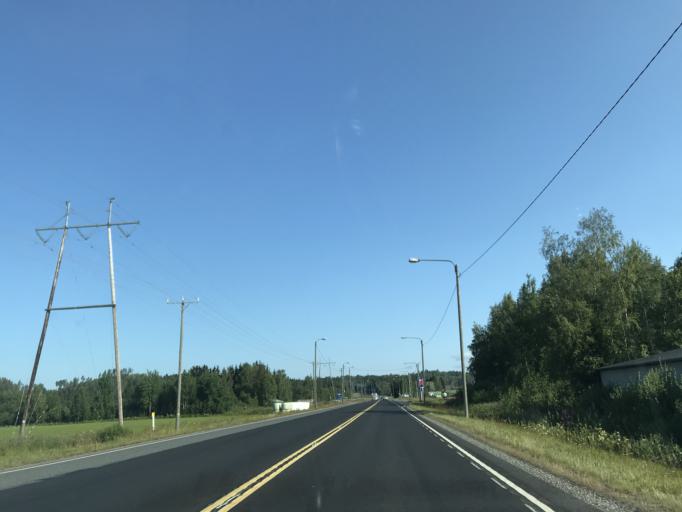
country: FI
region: Paijanne Tavastia
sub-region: Lahti
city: Lahti
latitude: 61.1209
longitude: 25.6402
